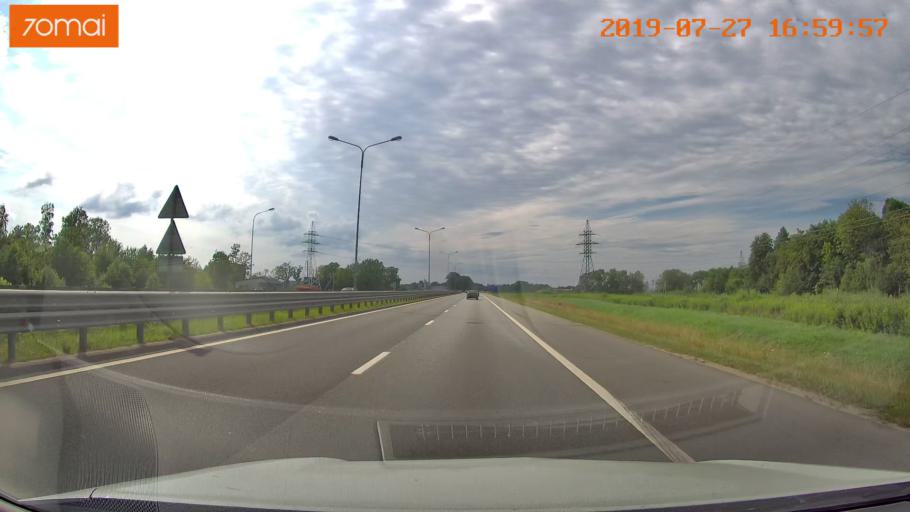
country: RU
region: Kaliningrad
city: Bol'shoe Isakovo
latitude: 54.7062
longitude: 20.6368
